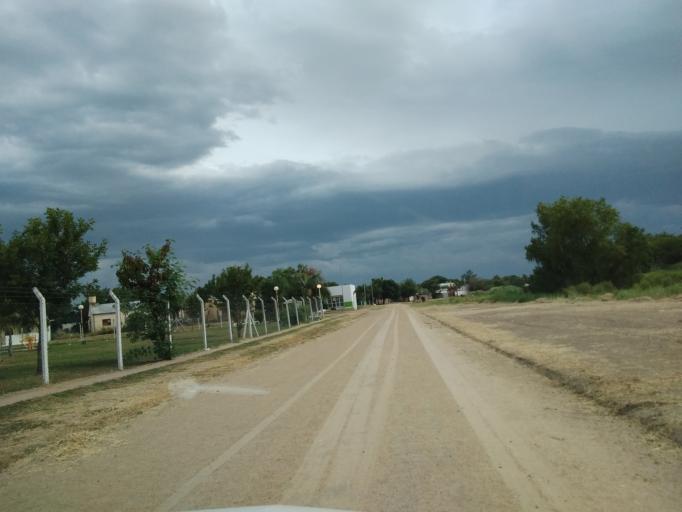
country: AR
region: Corrientes
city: Corrientes
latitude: -27.5188
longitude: -58.7934
